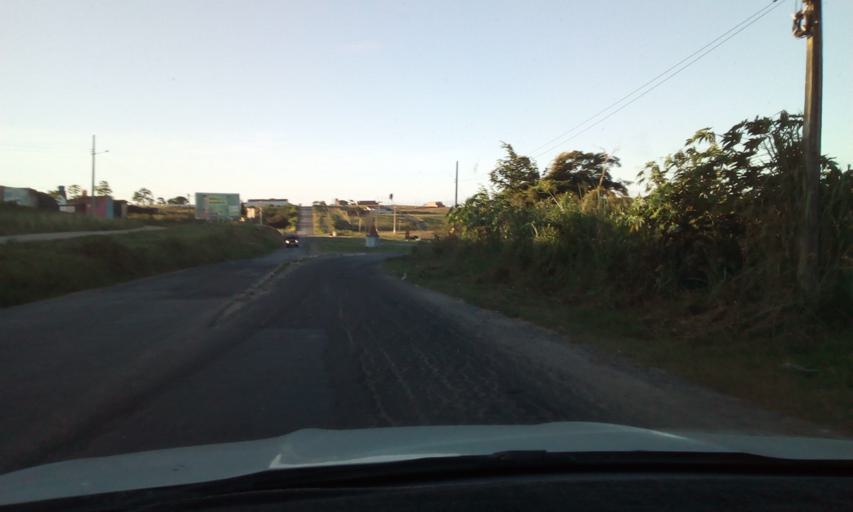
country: BR
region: Paraiba
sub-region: Areia
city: Remigio
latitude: -6.9618
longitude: -35.7922
